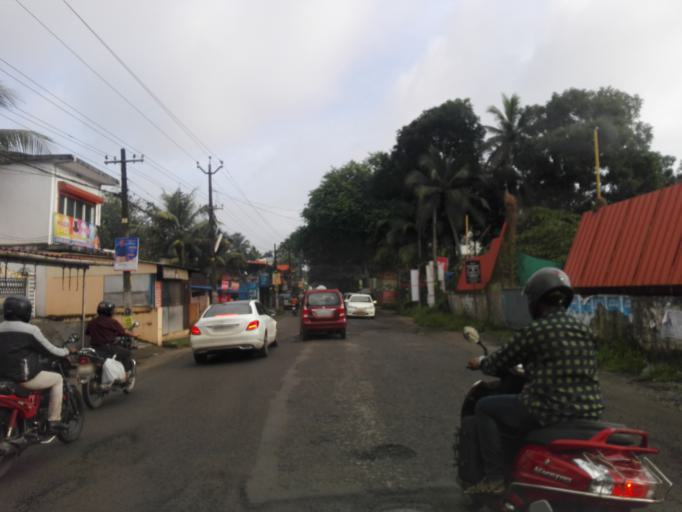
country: IN
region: Kerala
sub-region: Alappuzha
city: Arukutti
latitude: 9.9152
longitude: 76.3633
